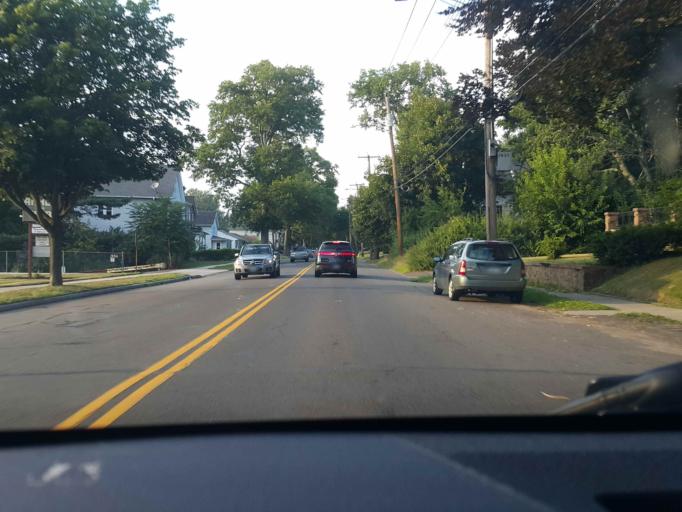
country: US
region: Connecticut
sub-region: New Haven County
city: East Haven
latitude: 41.2838
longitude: -72.8964
